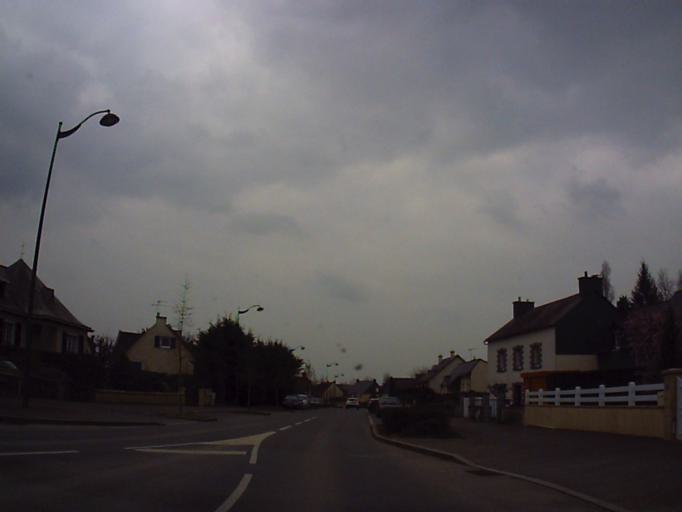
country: FR
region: Brittany
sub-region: Departement d'Ille-et-Vilaine
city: Breteil
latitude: 48.1445
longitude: -1.8927
